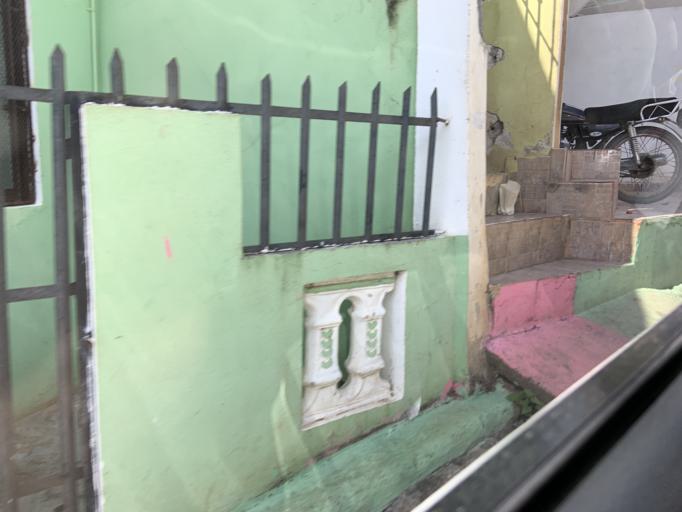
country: DO
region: Monte Plata
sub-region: Yamasa
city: Yamasa
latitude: 18.7730
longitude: -70.0280
